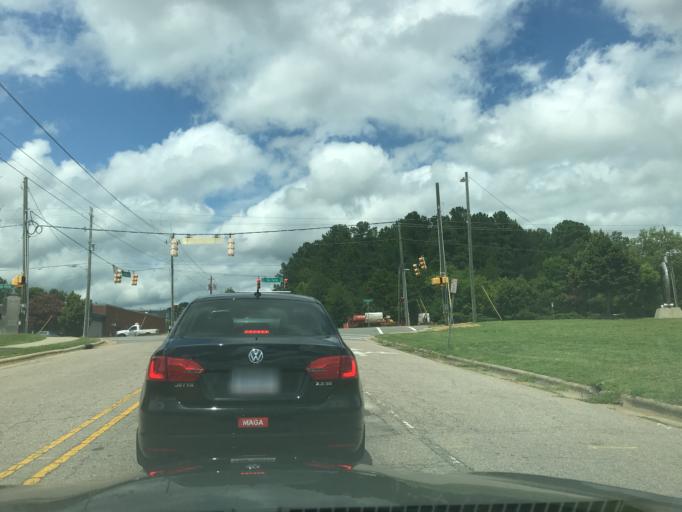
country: US
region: North Carolina
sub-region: Wake County
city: Raleigh
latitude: 35.8180
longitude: -78.6202
